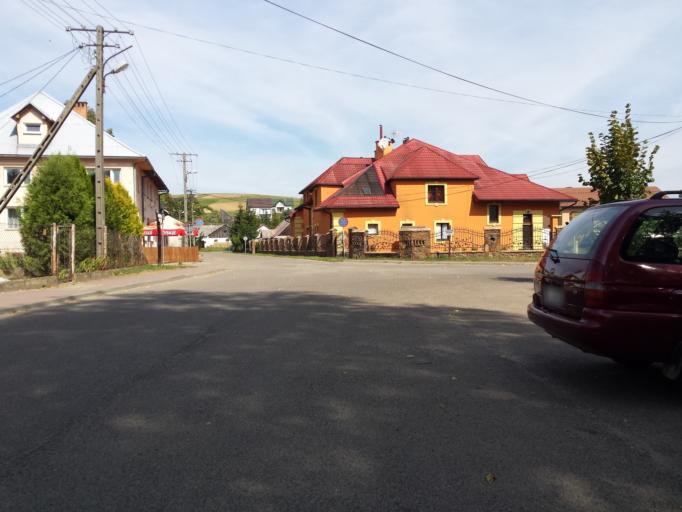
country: PL
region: Subcarpathian Voivodeship
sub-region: Powiat leski
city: Baligrod
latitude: 49.3369
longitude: 22.2858
